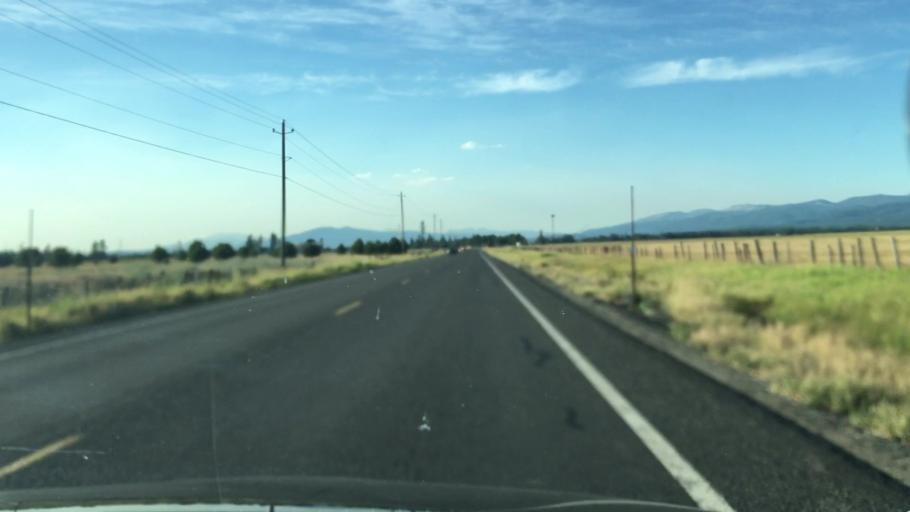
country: US
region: Idaho
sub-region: Valley County
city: McCall
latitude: 44.7646
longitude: -116.0783
